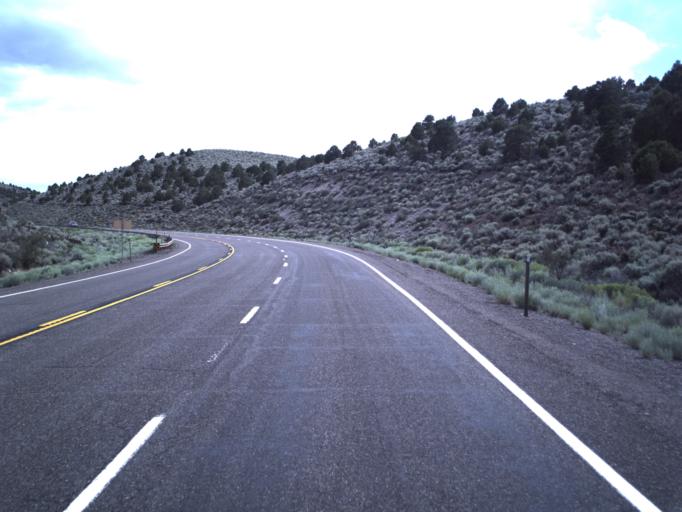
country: US
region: Utah
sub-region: Wayne County
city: Loa
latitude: 38.5224
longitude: -111.8333
